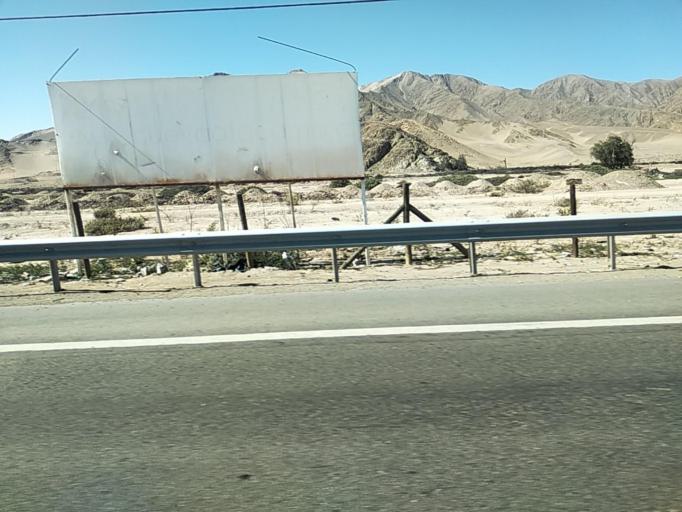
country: CL
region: Atacama
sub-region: Provincia de Copiapo
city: Copiapo
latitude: -27.3439
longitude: -70.3624
